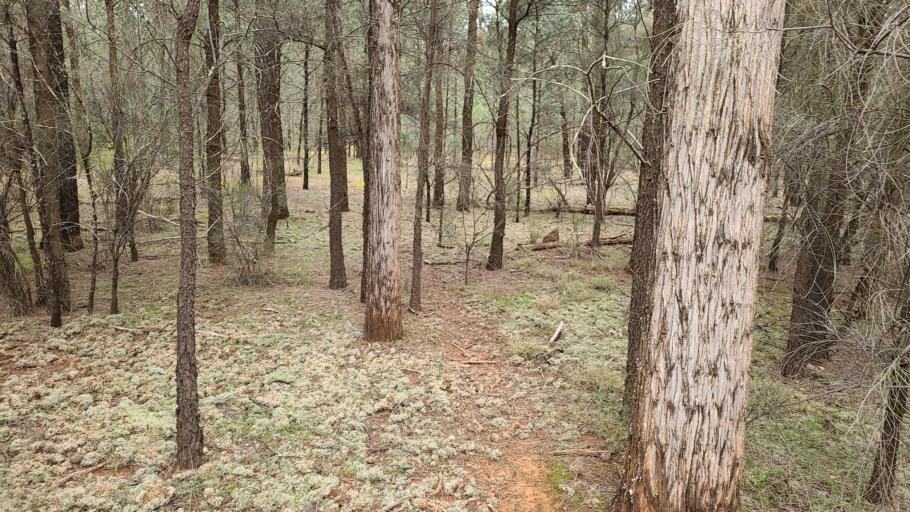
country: AU
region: New South Wales
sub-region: Coolamon
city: Coolamon
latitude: -34.8586
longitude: 146.9241
